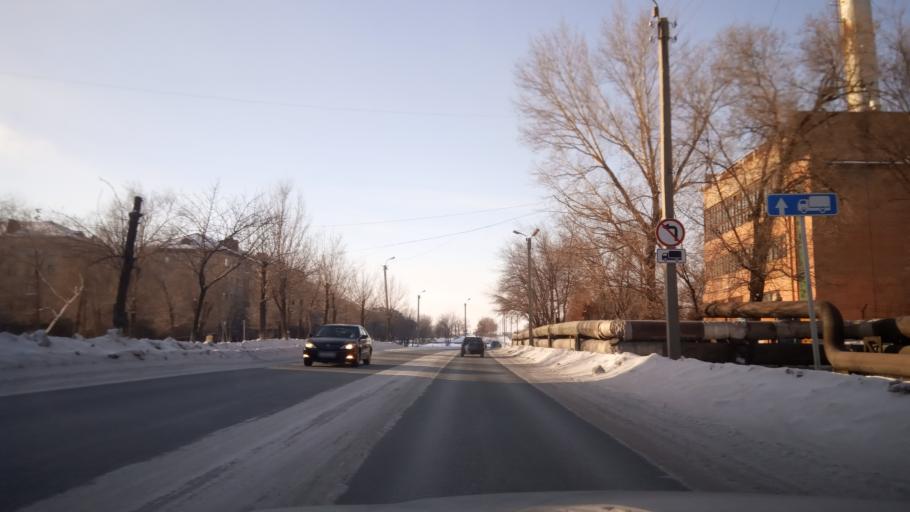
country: RU
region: Orenburg
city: Novotroitsk
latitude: 51.2004
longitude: 58.3089
